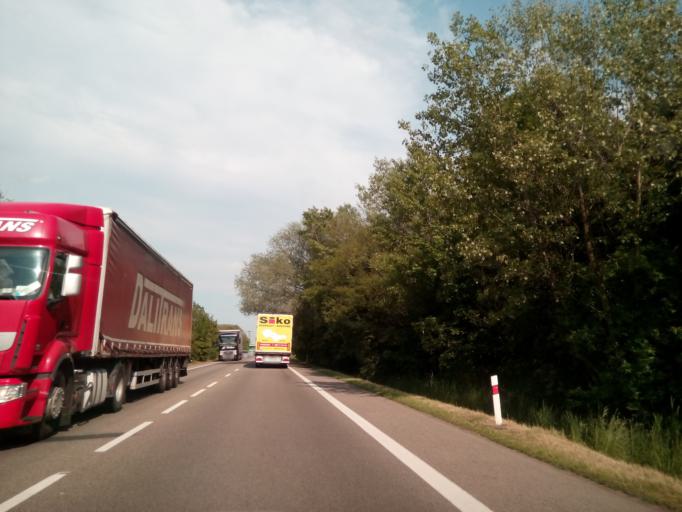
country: CZ
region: South Moravian
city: Slavkov u Brna
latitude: 49.1467
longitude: 16.8825
